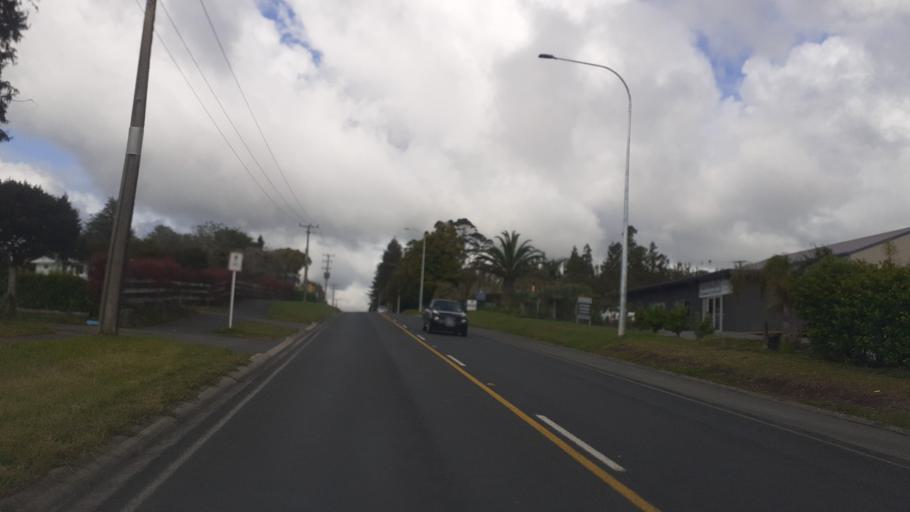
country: NZ
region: Northland
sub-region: Far North District
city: Kerikeri
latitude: -35.2367
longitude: 173.9410
